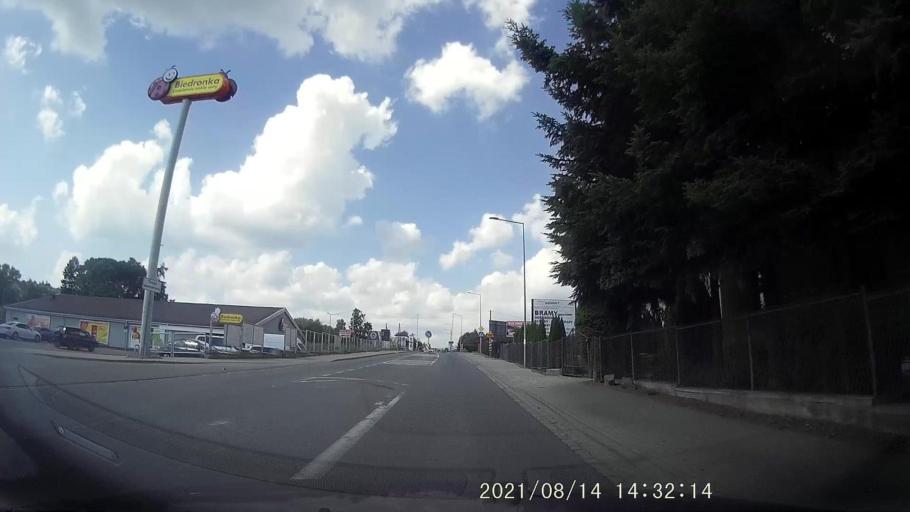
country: PL
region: Lower Silesian Voivodeship
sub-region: Powiat klodzki
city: Bozkow
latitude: 50.5483
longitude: 16.5506
